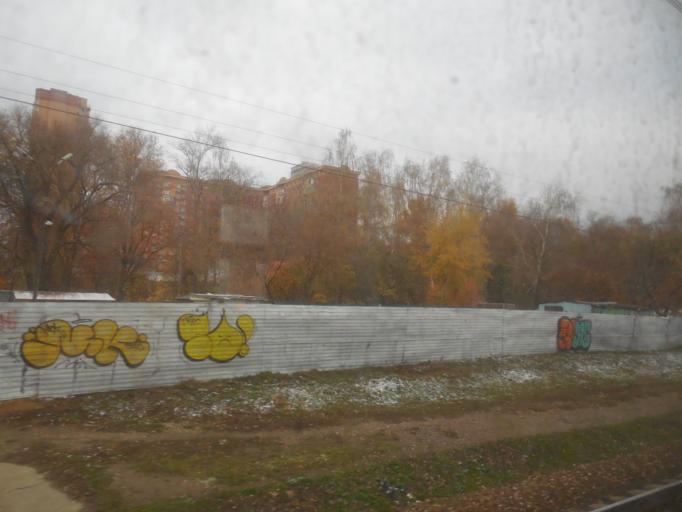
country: RU
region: Moskovskaya
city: Odintsovo
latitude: 55.6794
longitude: 37.2991
